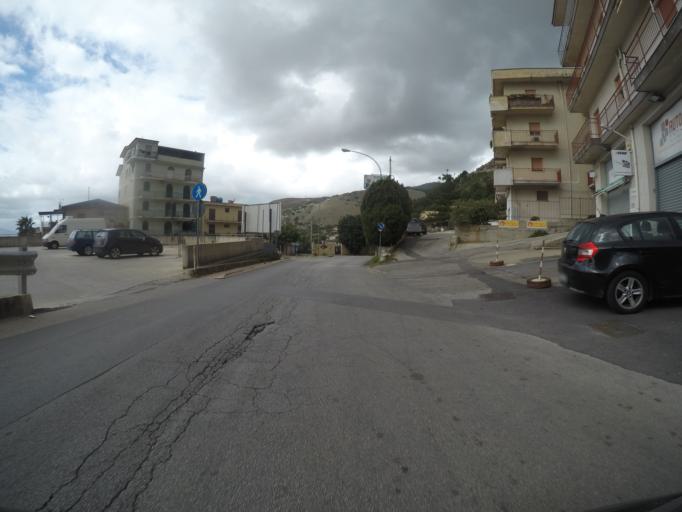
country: IT
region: Sicily
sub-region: Palermo
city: Montelepre
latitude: 38.0929
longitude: 13.1709
